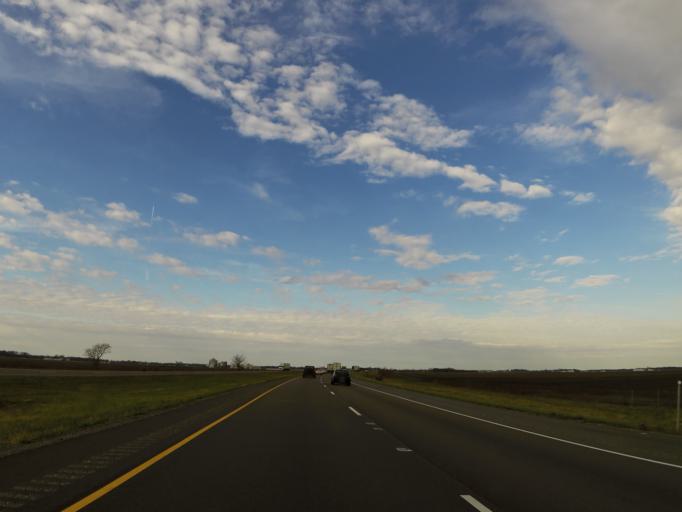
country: US
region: Illinois
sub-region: Washington County
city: Okawville
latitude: 38.4280
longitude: -89.4848
